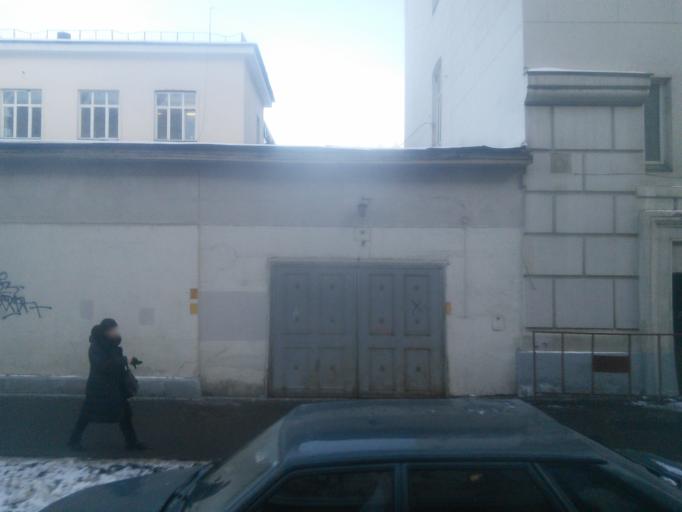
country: RU
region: Moscow
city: Lefortovo
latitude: 55.7648
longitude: 37.6827
